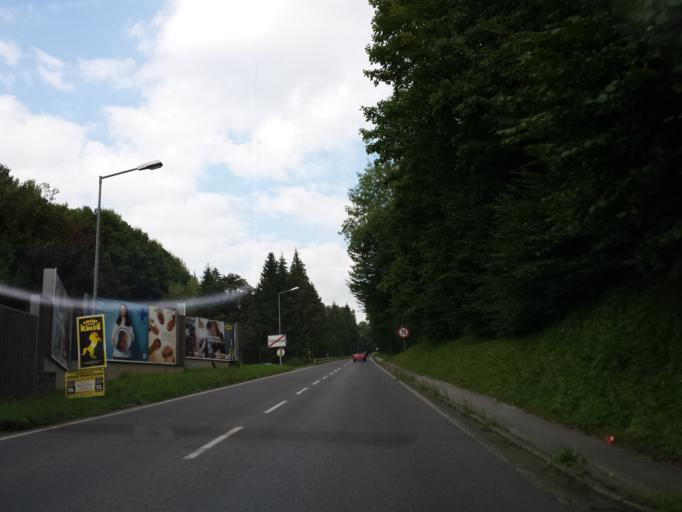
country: AT
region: Styria
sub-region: Politischer Bezirk Graz-Umgebung
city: Pirka
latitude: 46.9825
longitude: 15.3664
